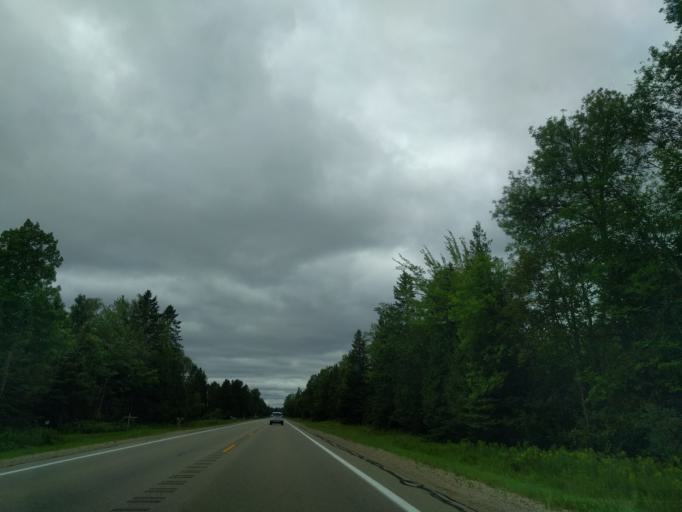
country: US
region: Michigan
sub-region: Delta County
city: Escanaba
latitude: 45.4681
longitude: -87.3173
